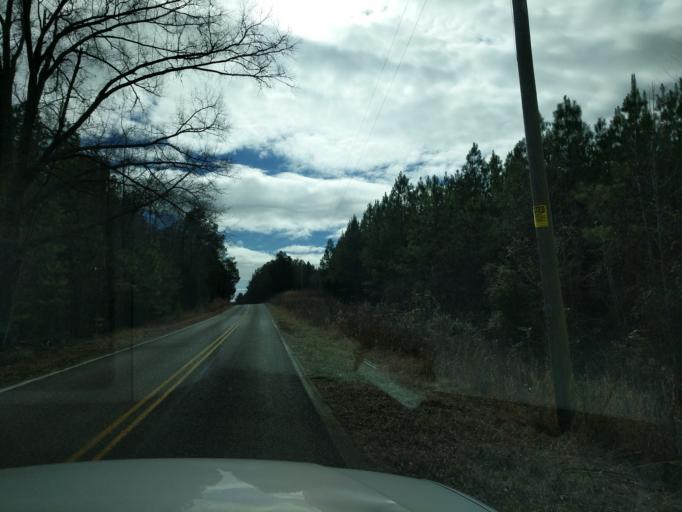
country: US
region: South Carolina
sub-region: Edgefield County
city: Edgefield
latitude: 33.9087
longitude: -82.0025
